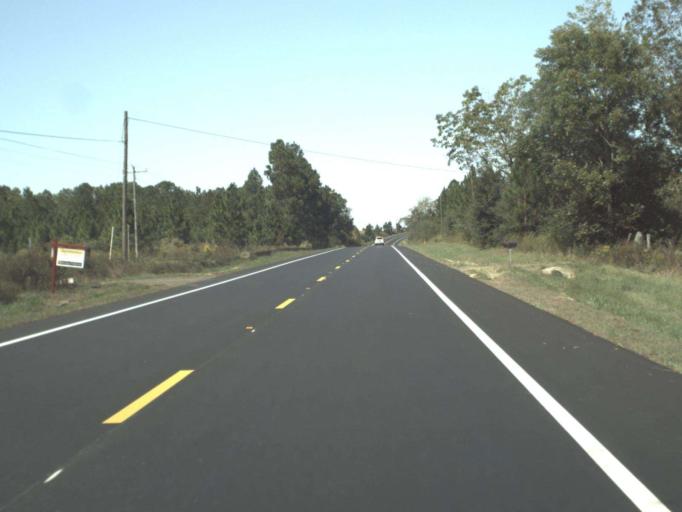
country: US
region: Alabama
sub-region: Covington County
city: Florala
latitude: 30.8828
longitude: -86.2727
